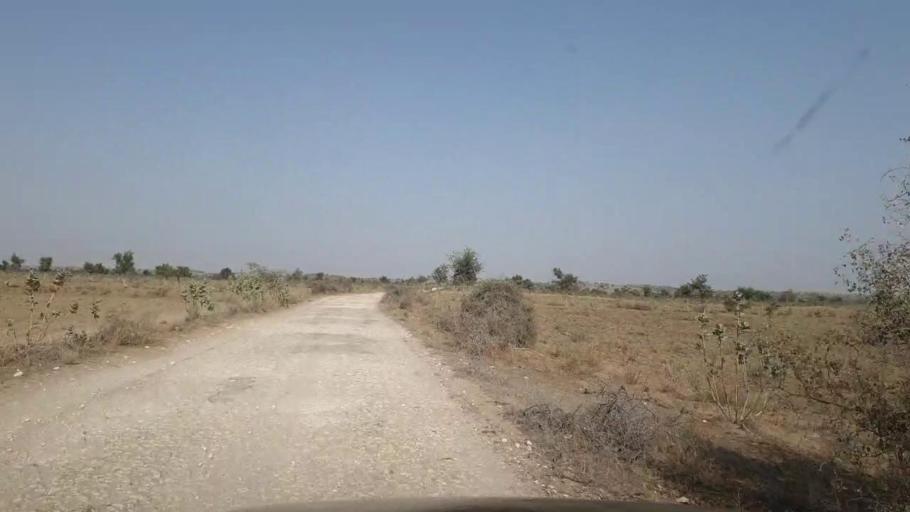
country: PK
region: Sindh
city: Islamkot
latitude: 25.0993
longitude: 70.4022
